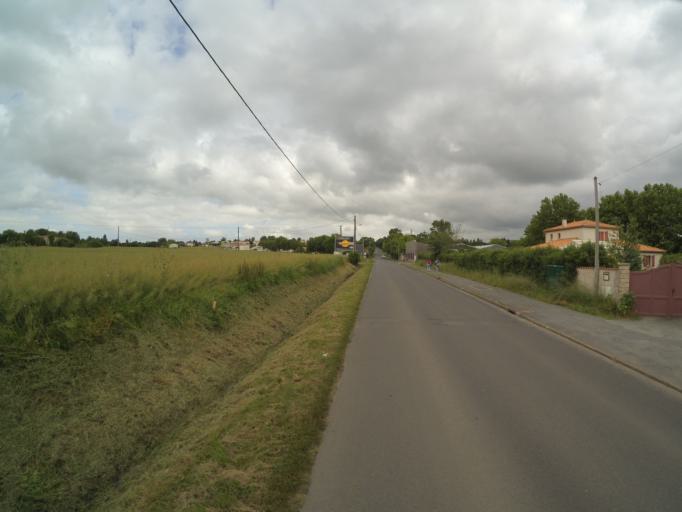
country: FR
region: Poitou-Charentes
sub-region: Departement de la Charente-Maritime
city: Breuil-Magne
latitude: 45.9605
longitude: -0.9697
